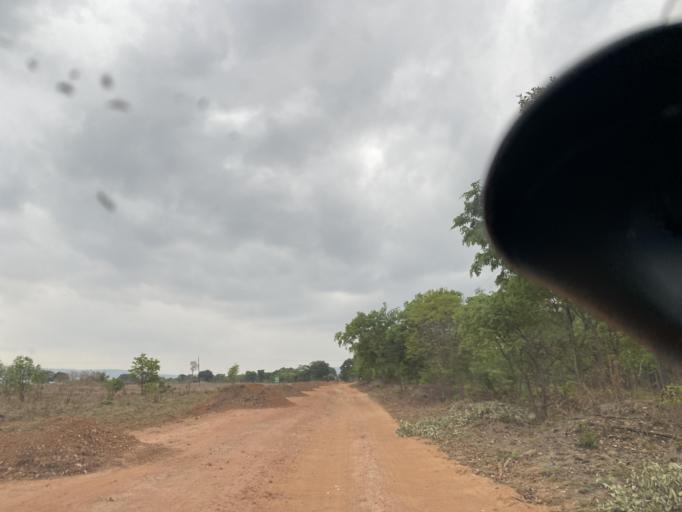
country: ZM
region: Lusaka
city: Chongwe
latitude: -15.2291
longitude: 28.7270
